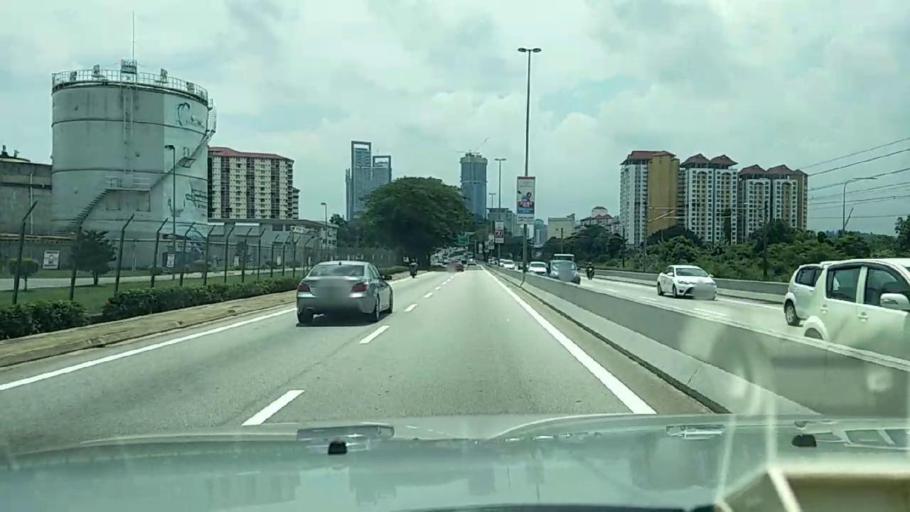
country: MY
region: Kuala Lumpur
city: Kuala Lumpur
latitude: 3.1021
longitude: 101.6716
